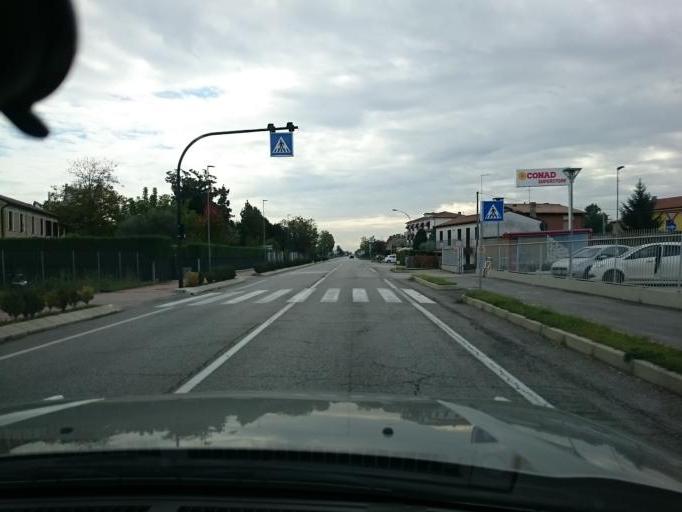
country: IT
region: Veneto
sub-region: Provincia di Padova
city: Legnaro
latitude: 45.3424
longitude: 11.9687
